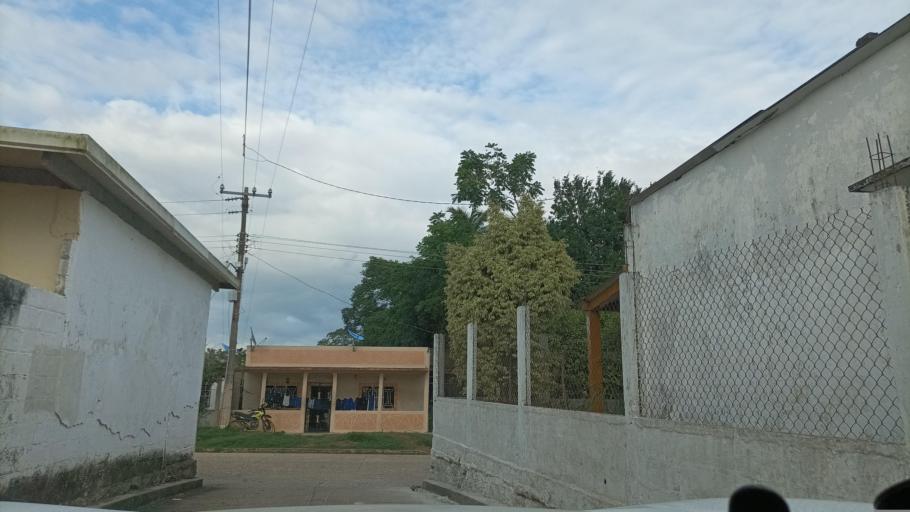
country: MX
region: Veracruz
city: Oluta
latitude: 17.8932
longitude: -94.8695
